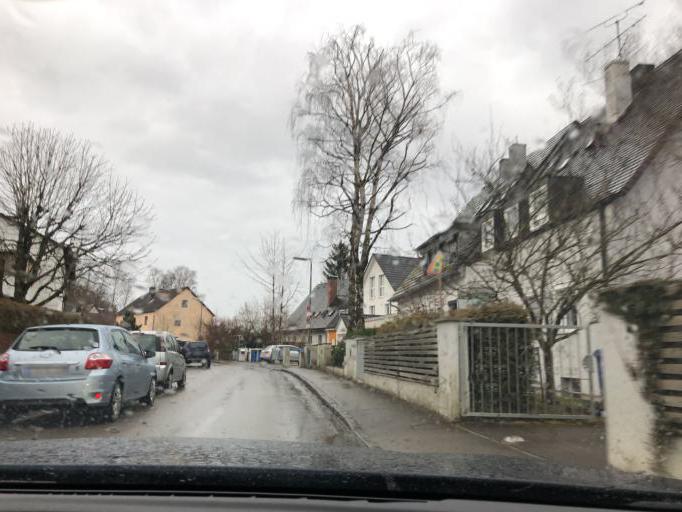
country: DE
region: Bavaria
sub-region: Upper Bavaria
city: Grobenzell
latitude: 48.1787
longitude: 11.3998
